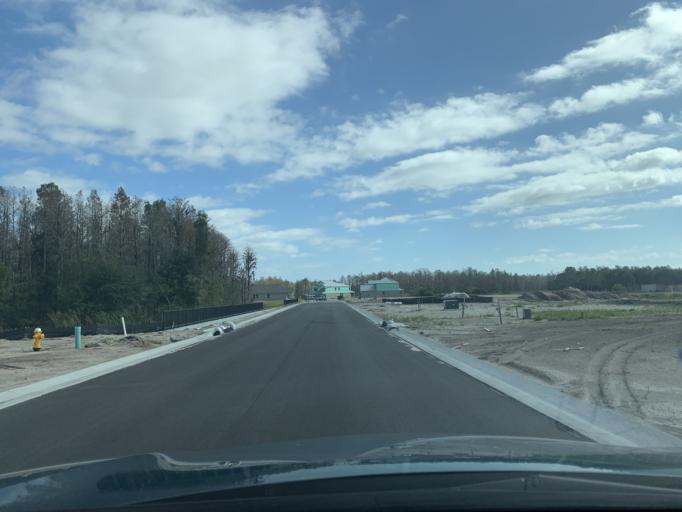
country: US
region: Florida
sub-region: Pasco County
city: Trinity
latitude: 28.1980
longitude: -82.6727
